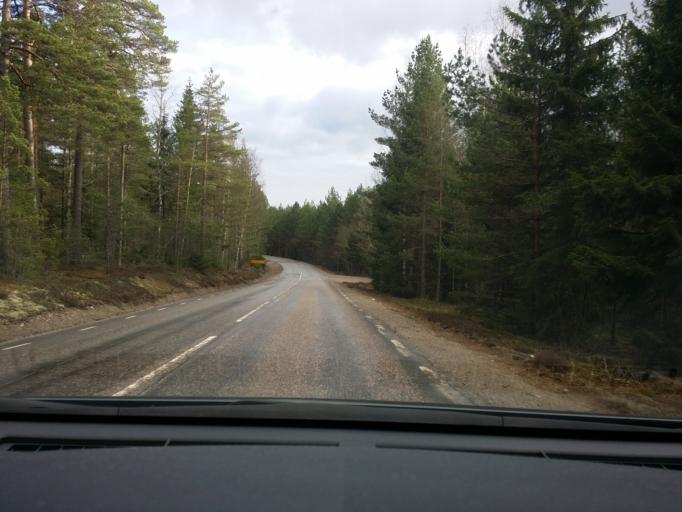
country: SE
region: Soedermanland
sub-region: Eskilstuna Kommun
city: Arla
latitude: 59.2998
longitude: 16.6768
